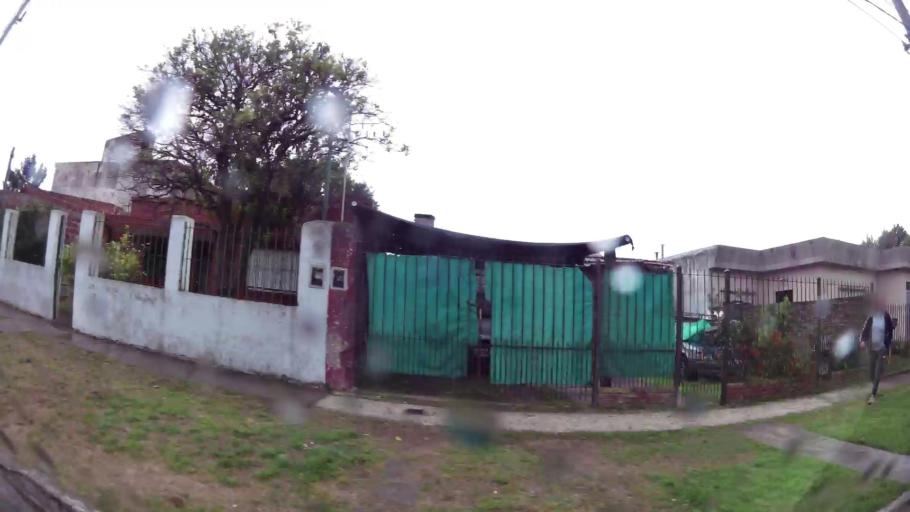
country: AR
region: Buenos Aires
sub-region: Partido de Quilmes
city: Quilmes
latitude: -34.7647
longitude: -58.2322
